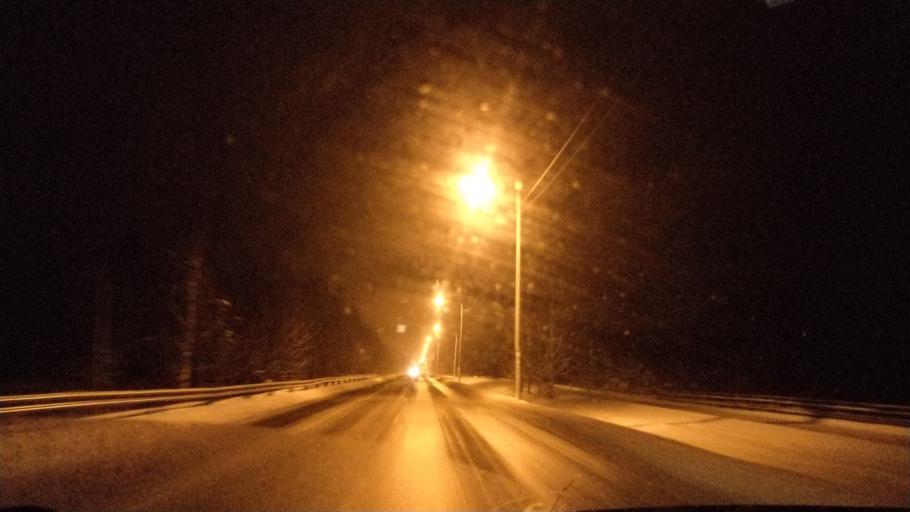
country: FI
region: Lapland
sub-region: Rovaniemi
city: Rovaniemi
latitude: 66.2844
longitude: 25.3398
